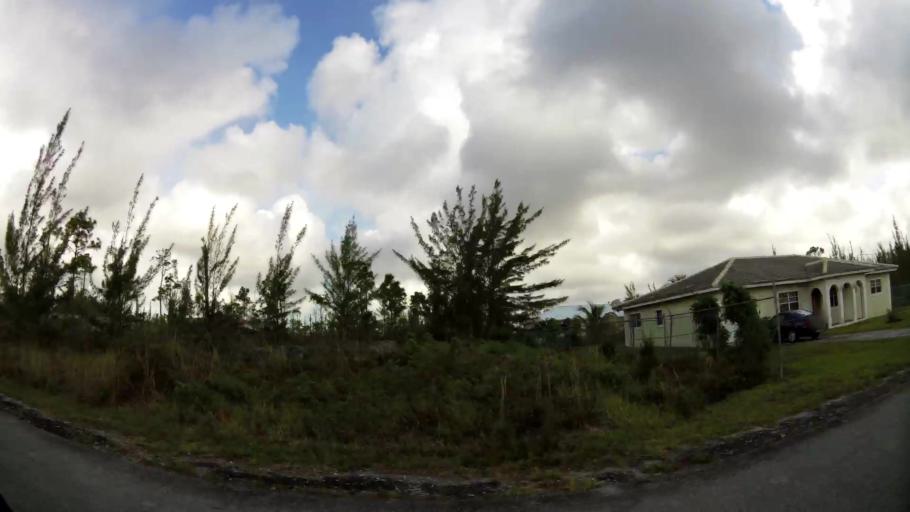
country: BS
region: Freeport
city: Lucaya
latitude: 26.5823
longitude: -78.5858
